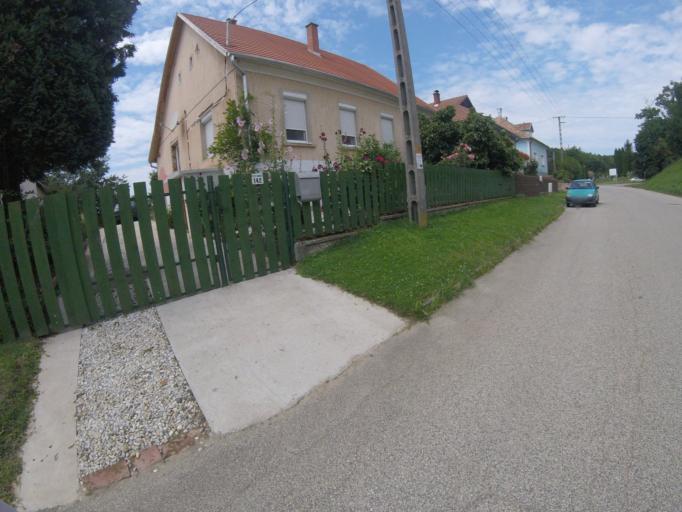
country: HR
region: Medimurska
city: Podturen
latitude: 46.5416
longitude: 16.5929
